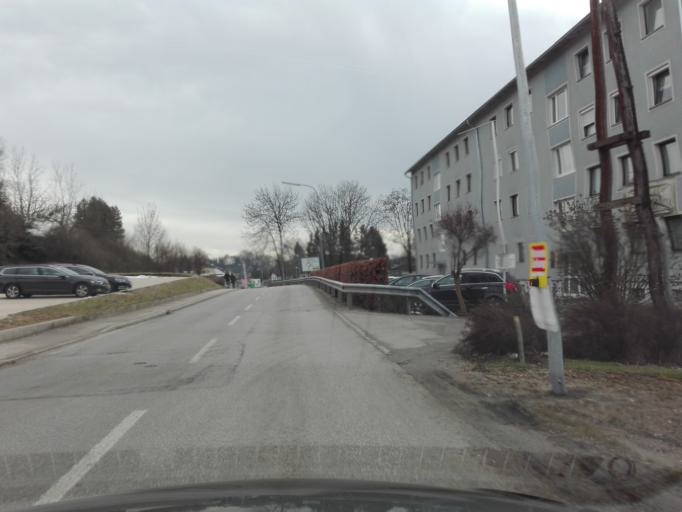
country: AT
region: Upper Austria
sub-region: Politischer Bezirk Perg
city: Perg
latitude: 48.2696
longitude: 14.5827
